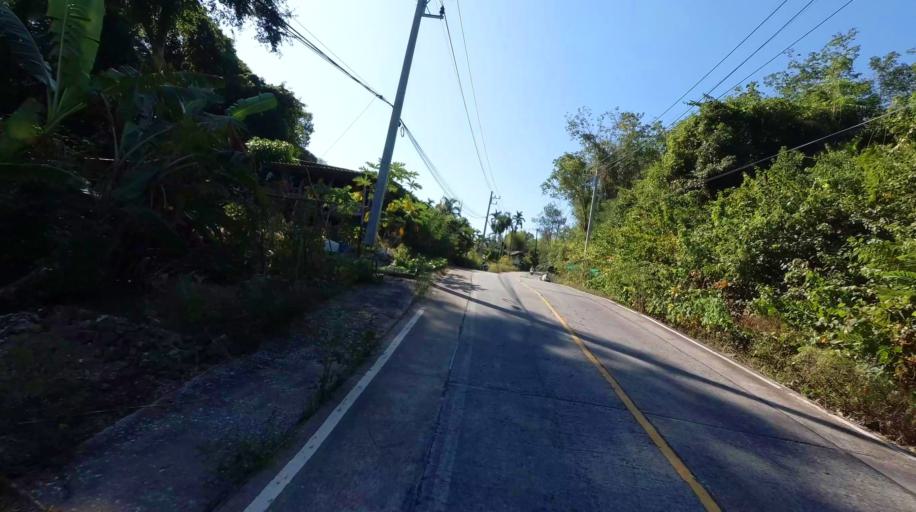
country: TH
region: Trat
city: Ko Kut
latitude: 11.6153
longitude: 102.5434
